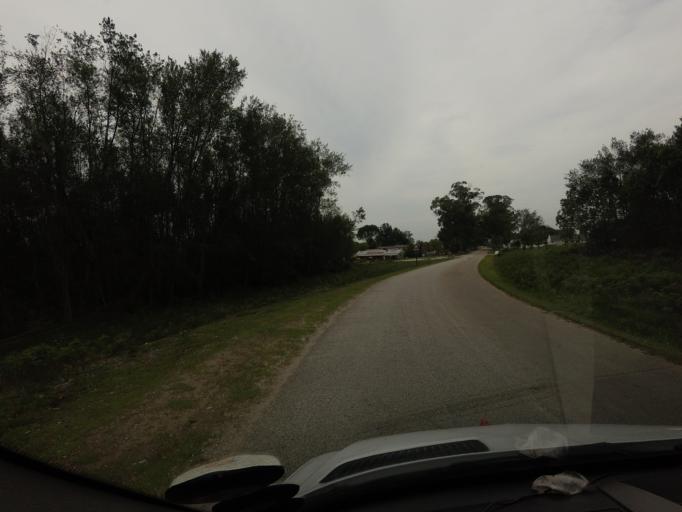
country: ZA
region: Eastern Cape
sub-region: Cacadu District Municipality
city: Kareedouw
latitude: -33.9700
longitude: 23.8879
